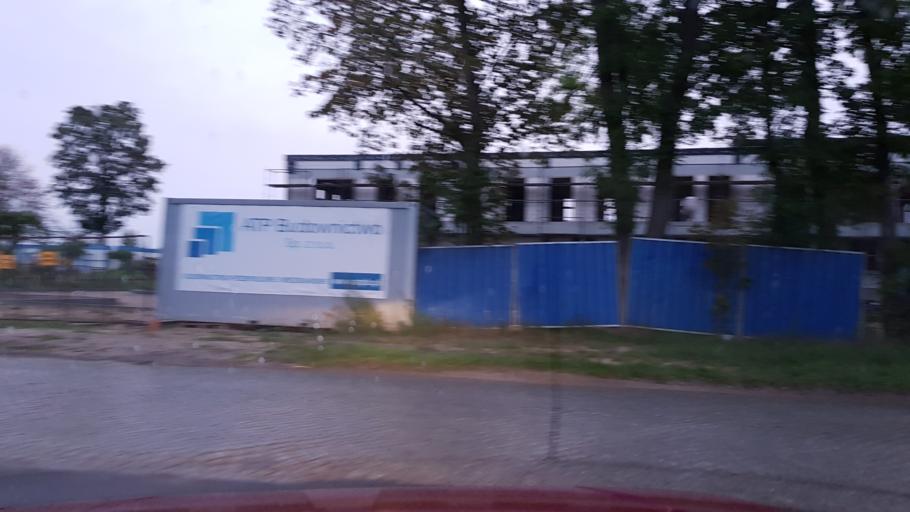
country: PL
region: West Pomeranian Voivodeship
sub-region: Powiat slawienski
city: Slawno
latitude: 54.3491
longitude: 16.6809
